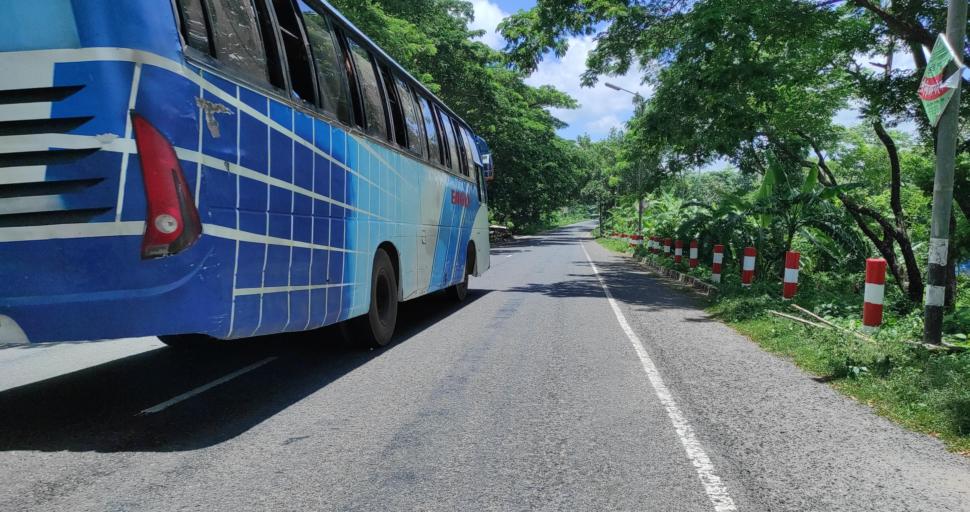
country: BD
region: Barisal
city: Barisal
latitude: 22.8223
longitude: 90.2667
